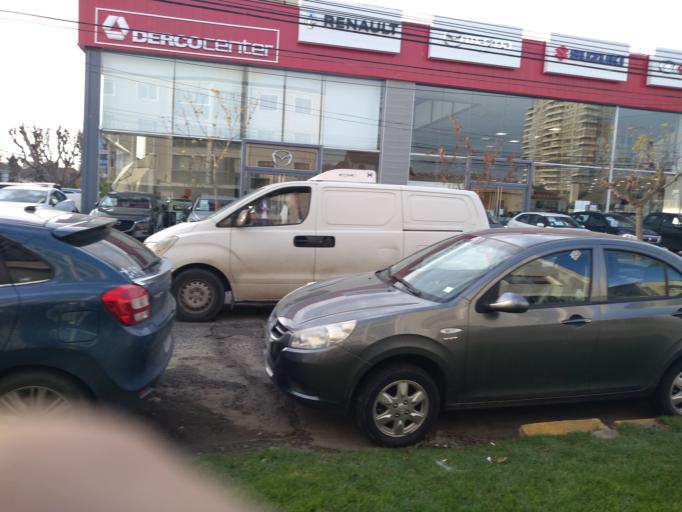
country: CL
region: Valparaiso
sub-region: Provincia de Valparaiso
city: Vina del Mar
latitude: -33.0215
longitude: -71.5445
